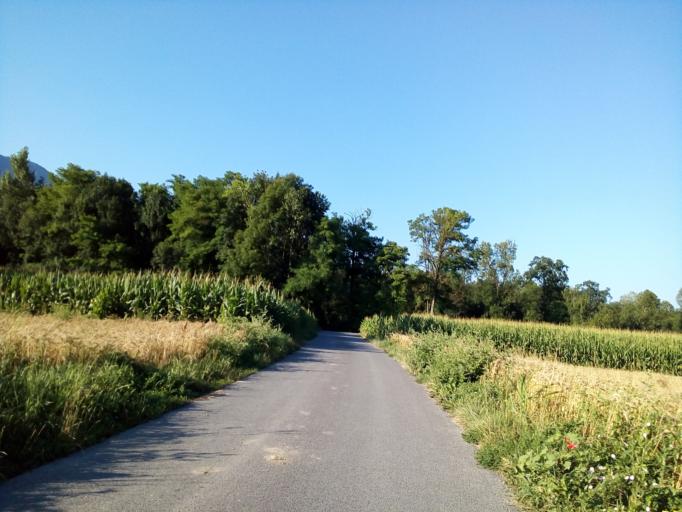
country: FR
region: Rhone-Alpes
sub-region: Departement de l'Isere
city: Goncelin
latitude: 45.3577
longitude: 5.9674
